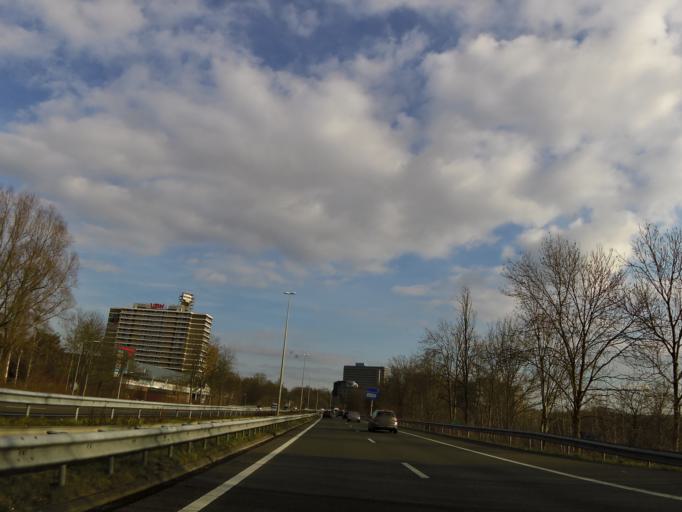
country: NL
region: Limburg
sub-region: Gemeente Heerlen
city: Heerlen
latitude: 50.8868
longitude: 5.9658
